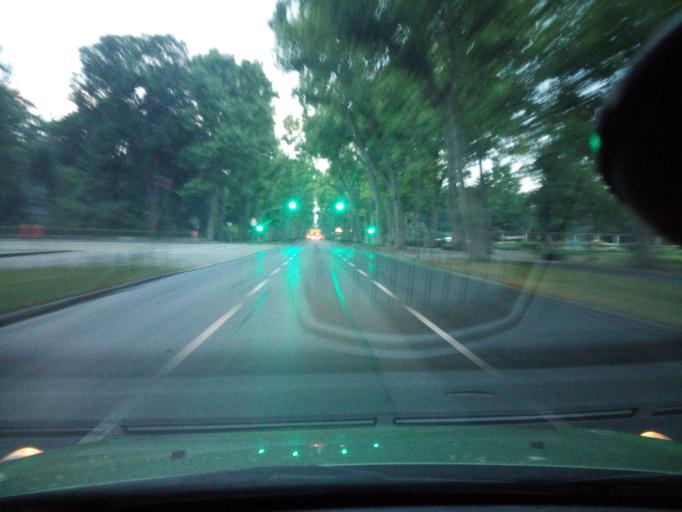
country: DE
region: Berlin
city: Plaenterwald
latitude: 52.4902
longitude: 13.4709
